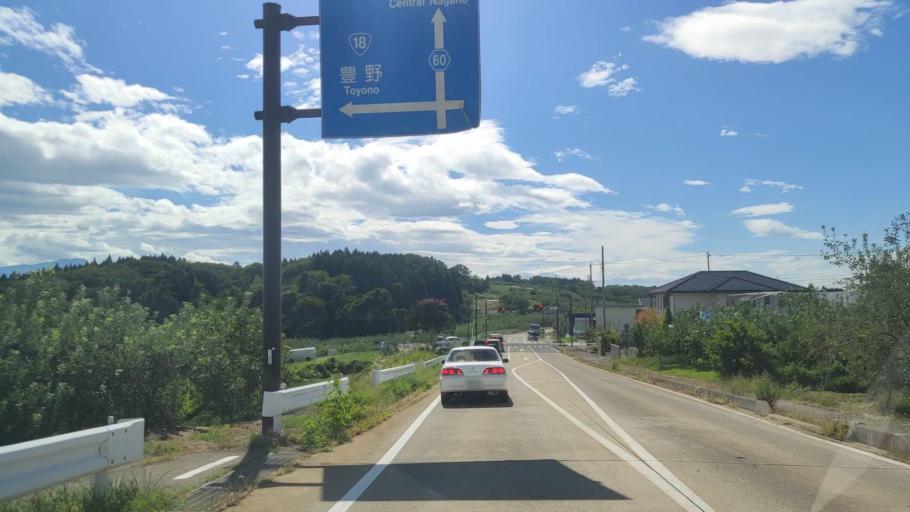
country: JP
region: Nagano
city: Nagano-shi
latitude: 36.7060
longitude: 138.2462
